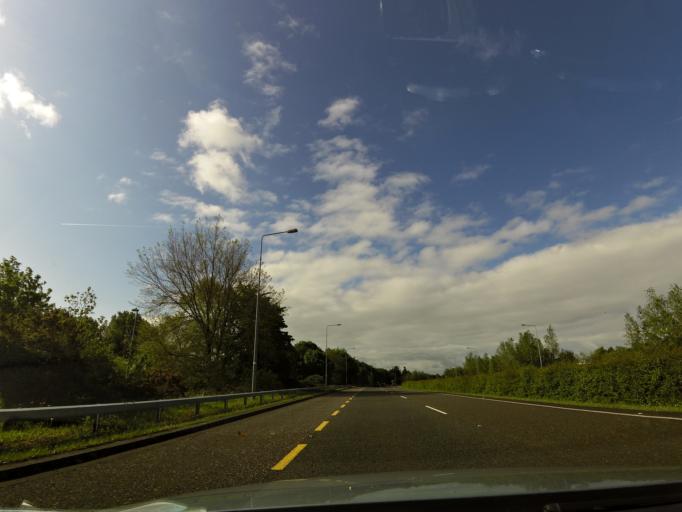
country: IE
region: Munster
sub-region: An Clar
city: Shannon
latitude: 52.7076
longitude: -8.8893
